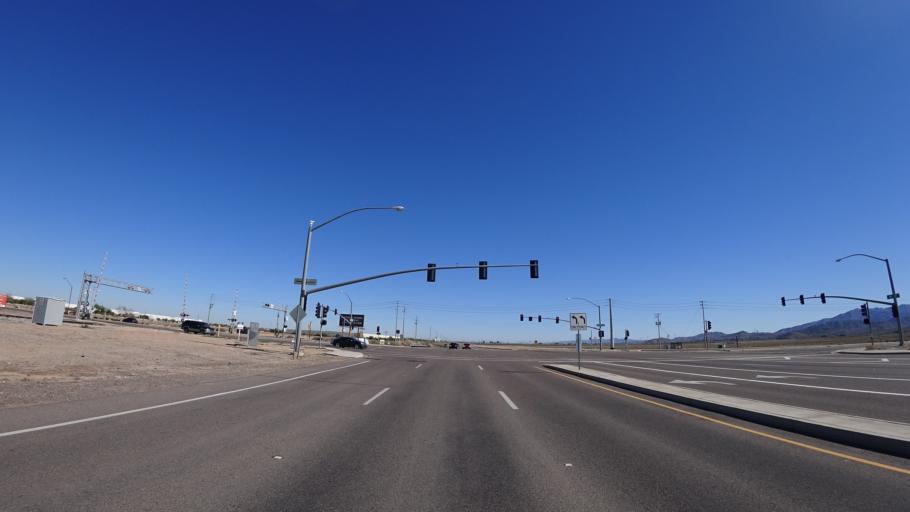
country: US
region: Arizona
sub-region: Maricopa County
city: Goodyear
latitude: 33.4043
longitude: -112.4274
